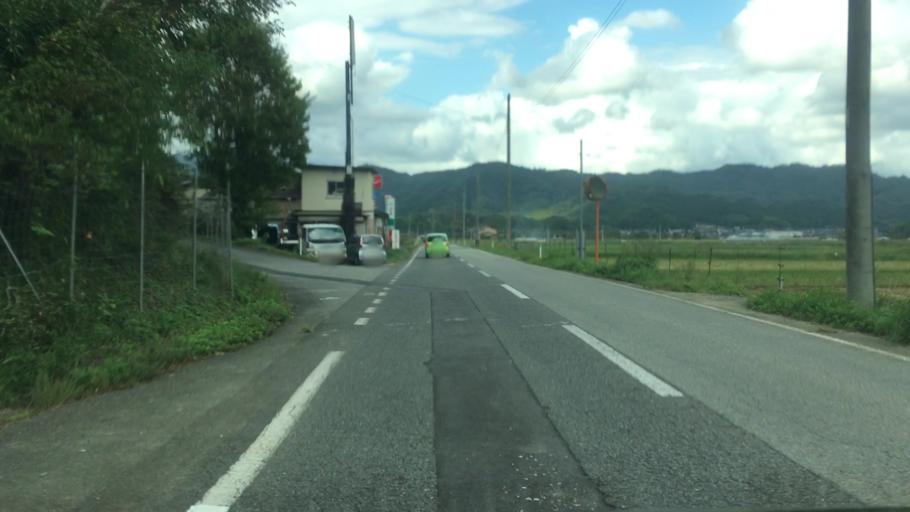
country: JP
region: Hyogo
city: Toyooka
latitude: 35.4464
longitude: 134.7298
